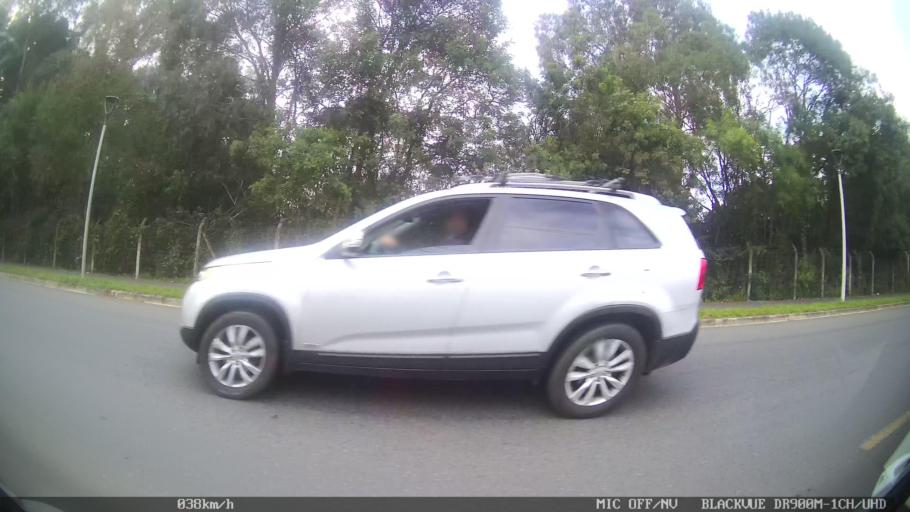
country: BR
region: Parana
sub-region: Almirante Tamandare
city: Almirante Tamandare
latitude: -25.3875
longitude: -49.3271
